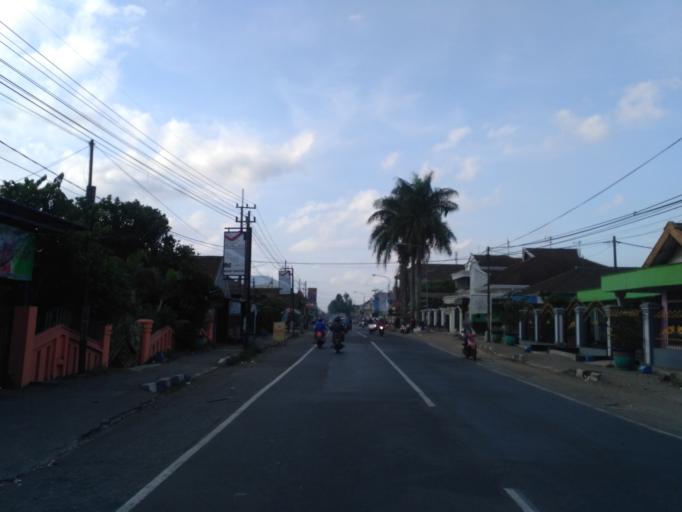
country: ID
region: East Java
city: Pakisaji
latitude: -8.0691
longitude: 112.5971
